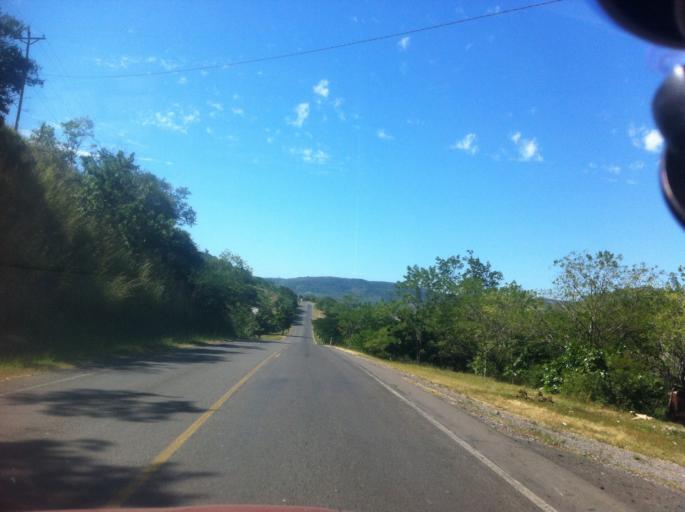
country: NI
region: Boaco
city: Teustepe
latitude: 12.3568
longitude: -85.8914
